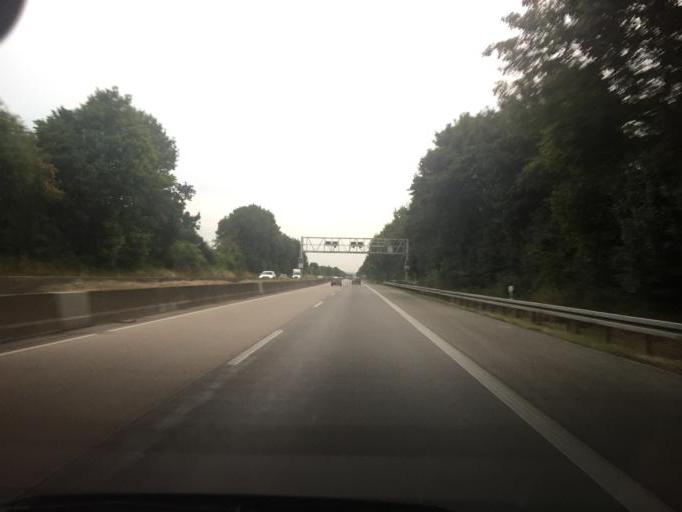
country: DE
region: North Rhine-Westphalia
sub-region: Regierungsbezirk Koln
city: Bedburg
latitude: 51.0113
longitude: 6.5014
